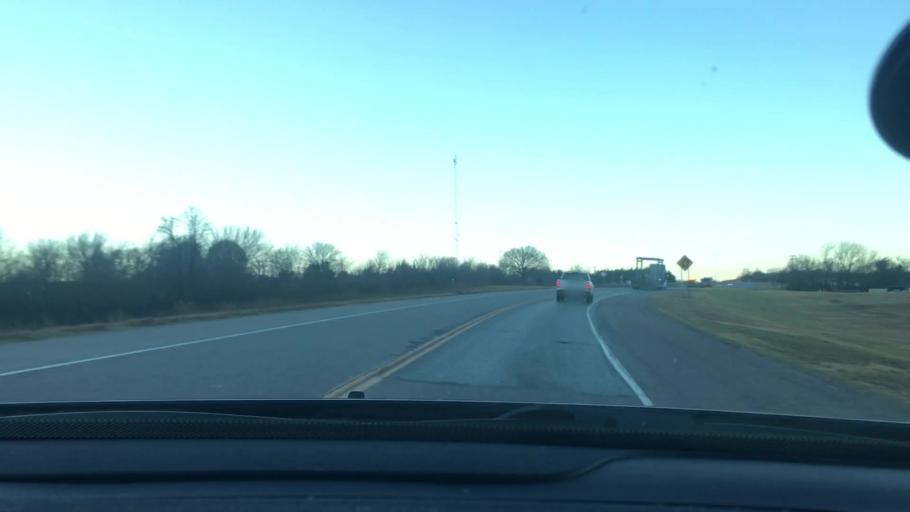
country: US
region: Oklahoma
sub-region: Pontotoc County
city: Ada
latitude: 34.7499
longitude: -96.7021
